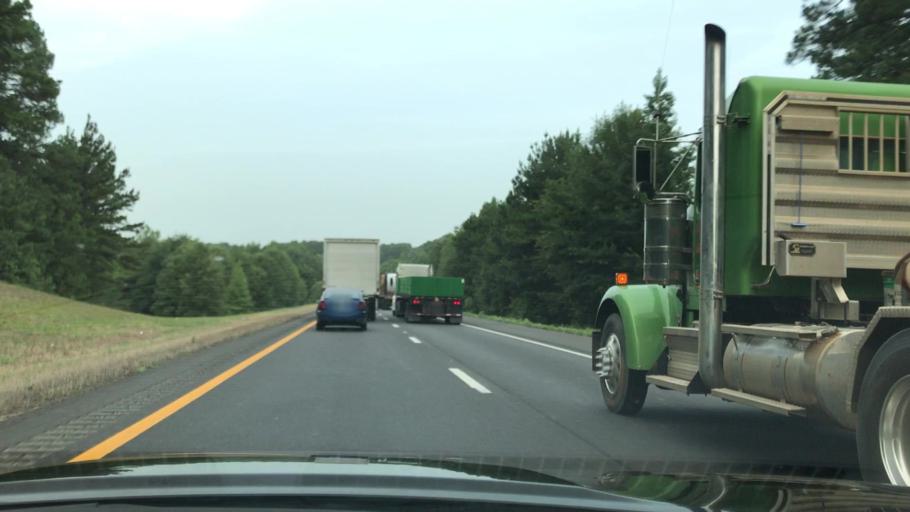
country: US
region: Texas
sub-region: Harrison County
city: Marshall
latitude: 32.4882
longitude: -94.4393
